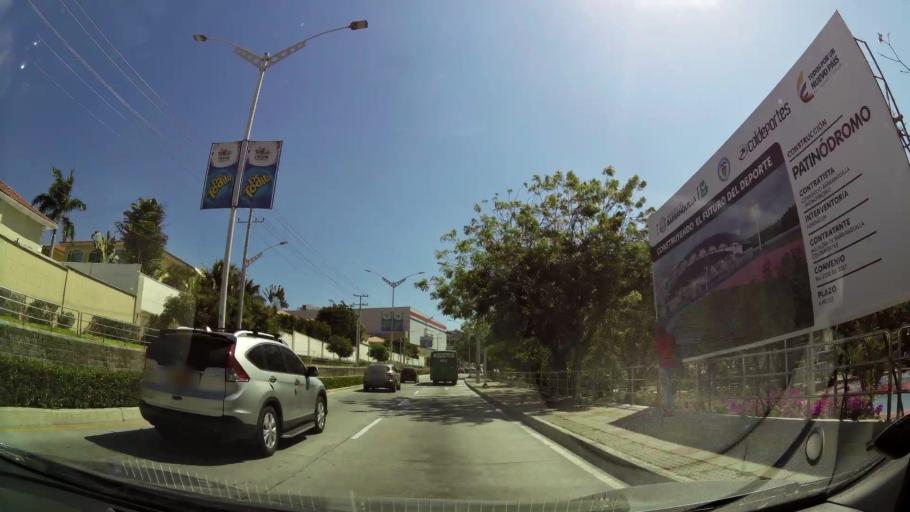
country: CO
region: Atlantico
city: Barranquilla
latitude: 11.0115
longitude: -74.8301
